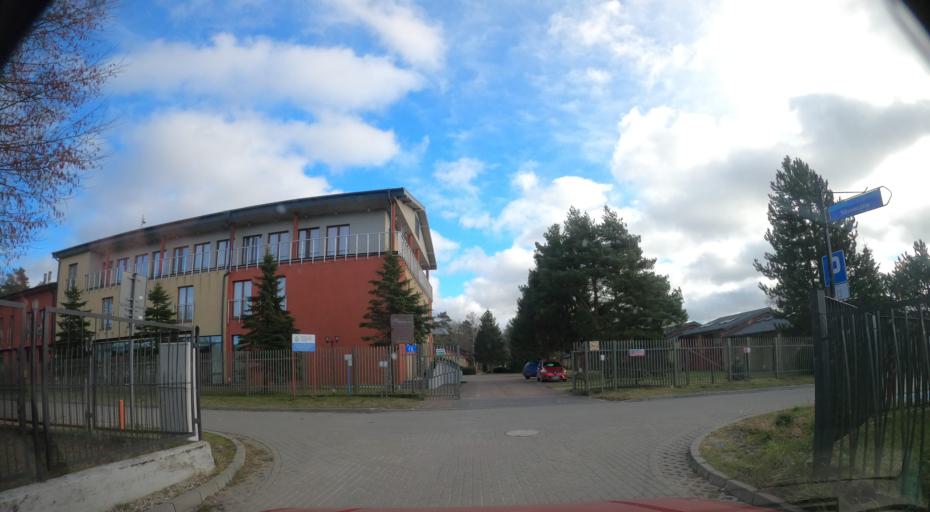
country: PL
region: West Pomeranian Voivodeship
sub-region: Powiat koszalinski
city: Sianow
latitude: 54.3132
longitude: 16.2074
